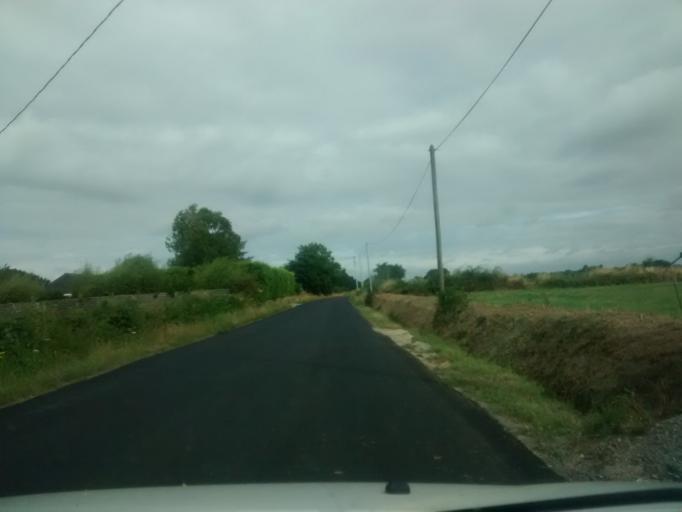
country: FR
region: Brittany
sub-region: Departement d'Ille-et-Vilaine
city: Saint-Jacques-de-la-Lande
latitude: 48.0870
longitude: -1.7357
